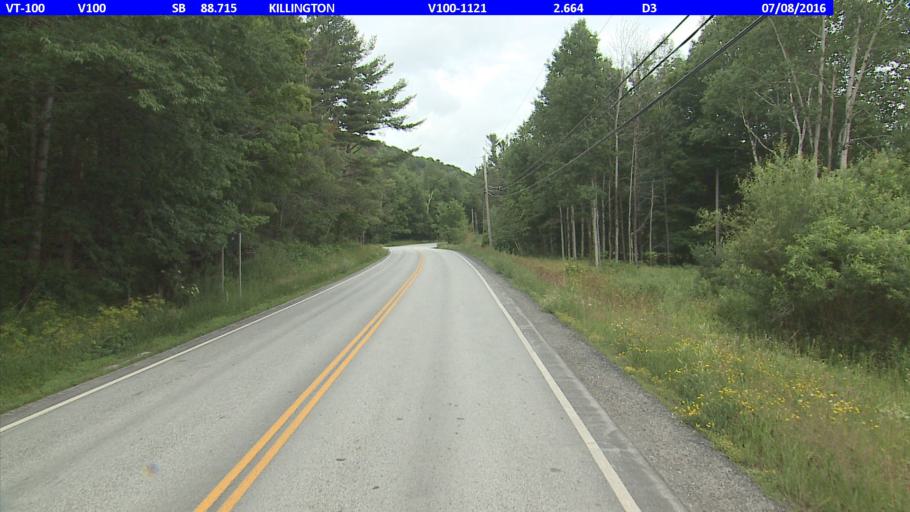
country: US
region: Vermont
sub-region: Rutland County
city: Rutland
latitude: 43.7013
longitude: -72.8197
